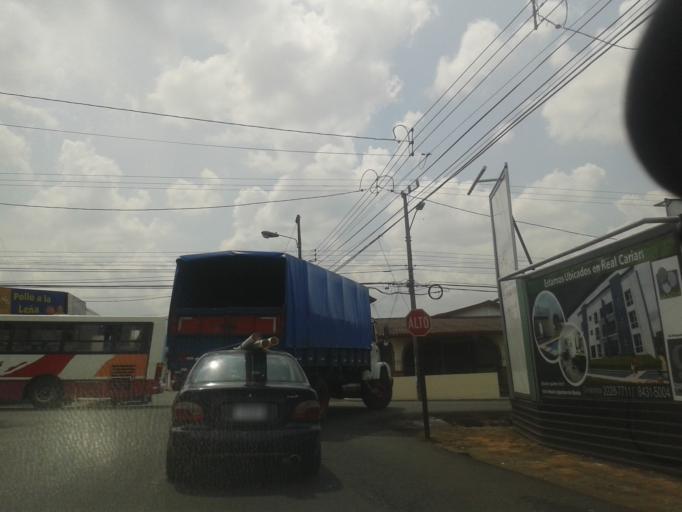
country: CR
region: Heredia
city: San Pablo
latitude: 9.9785
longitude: -84.0900
